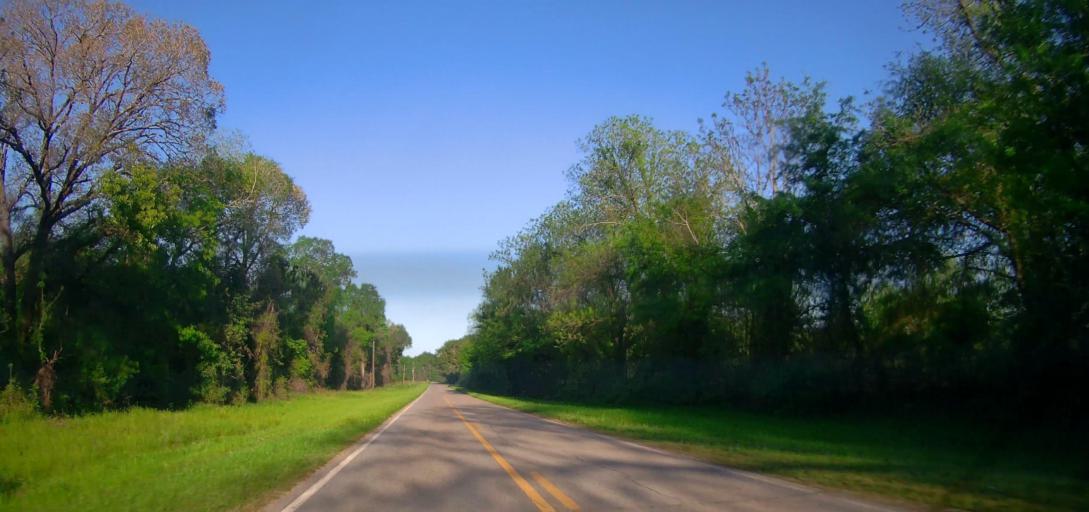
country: US
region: Georgia
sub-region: Macon County
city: Oglethorpe
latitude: 32.3053
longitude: -84.1116
